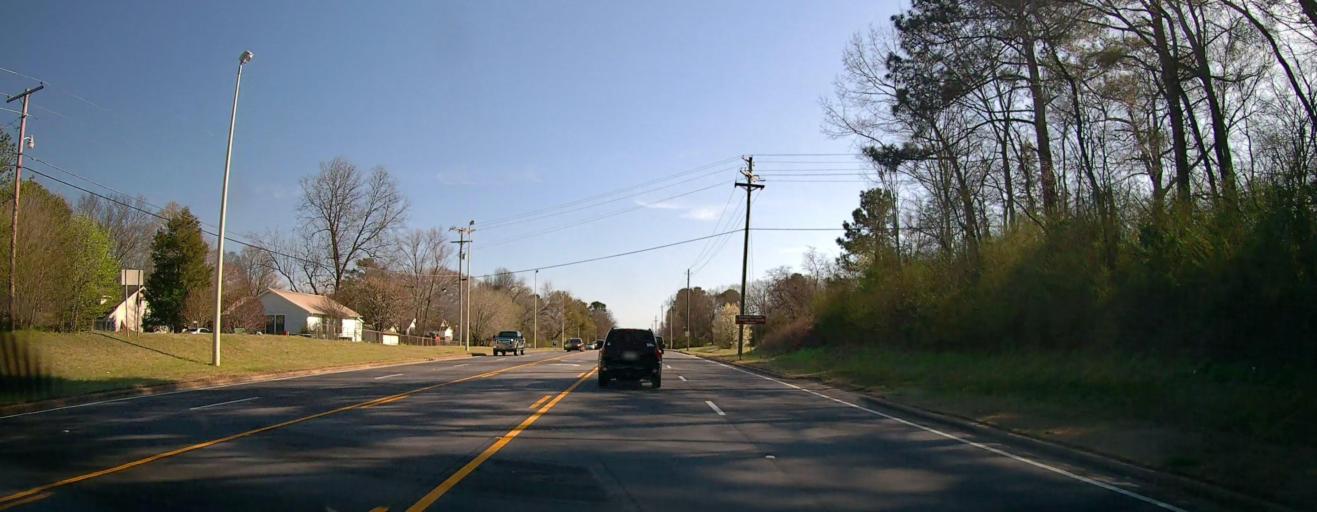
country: US
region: Alabama
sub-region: Lauderdale County
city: East Florence
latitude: 34.8213
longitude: -87.6265
